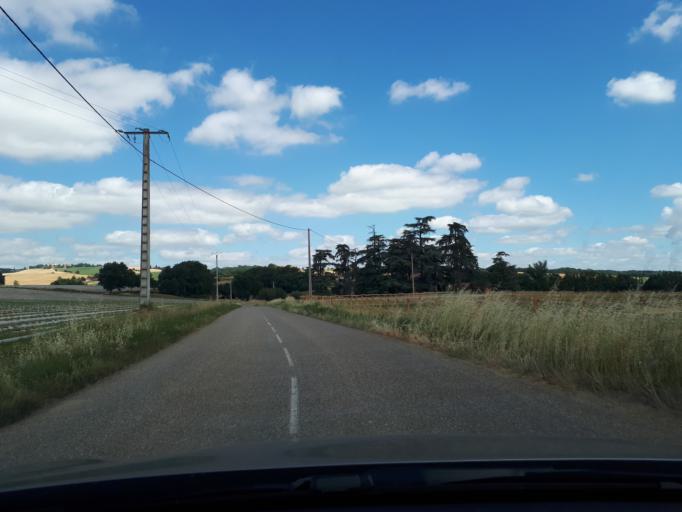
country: FR
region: Midi-Pyrenees
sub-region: Departement du Tarn-et-Garonne
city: Auvillar
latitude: 43.9989
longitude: 0.8196
